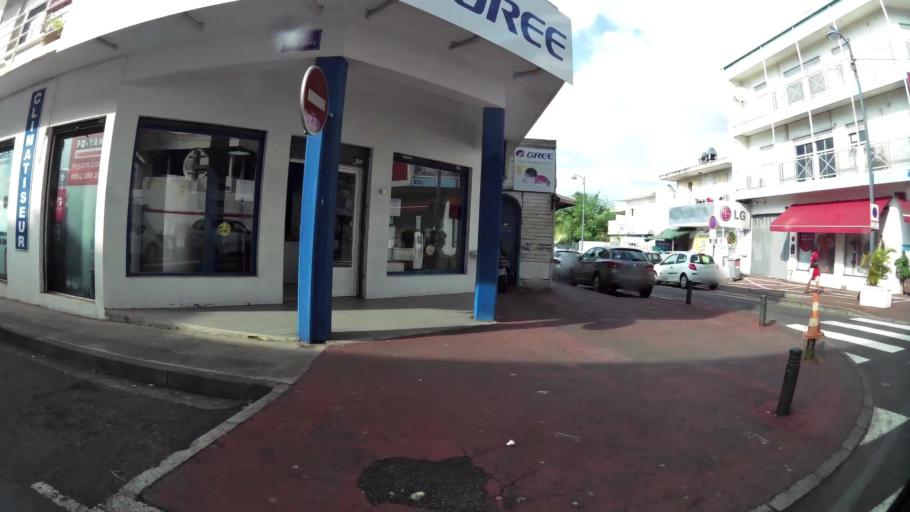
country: RE
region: Reunion
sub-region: Reunion
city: Saint-Denis
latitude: -20.8779
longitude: 55.4540
